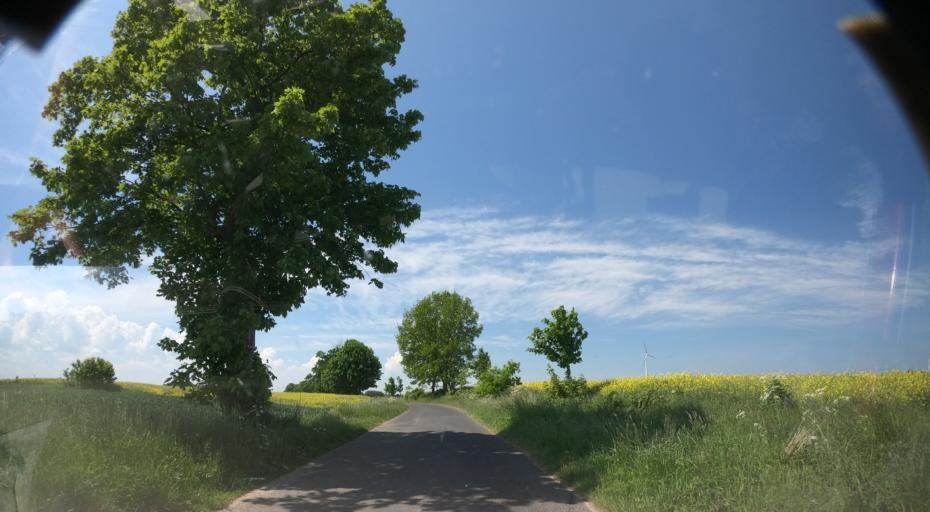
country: PL
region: West Pomeranian Voivodeship
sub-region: Powiat kolobrzeski
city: Ustronie Morskie
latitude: 54.1599
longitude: 15.8077
